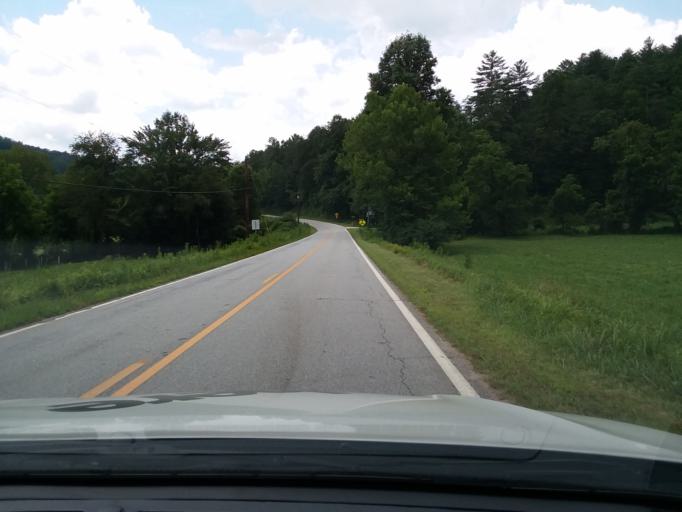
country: US
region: Georgia
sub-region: Rabun County
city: Mountain City
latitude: 34.9016
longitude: -83.2719
